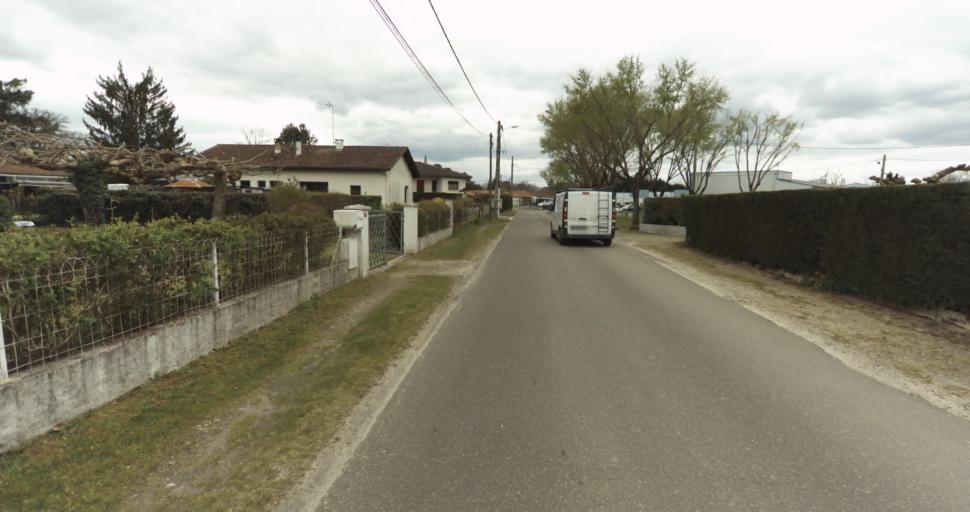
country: FR
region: Aquitaine
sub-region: Departement des Landes
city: Roquefort
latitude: 44.0370
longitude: -0.3136
